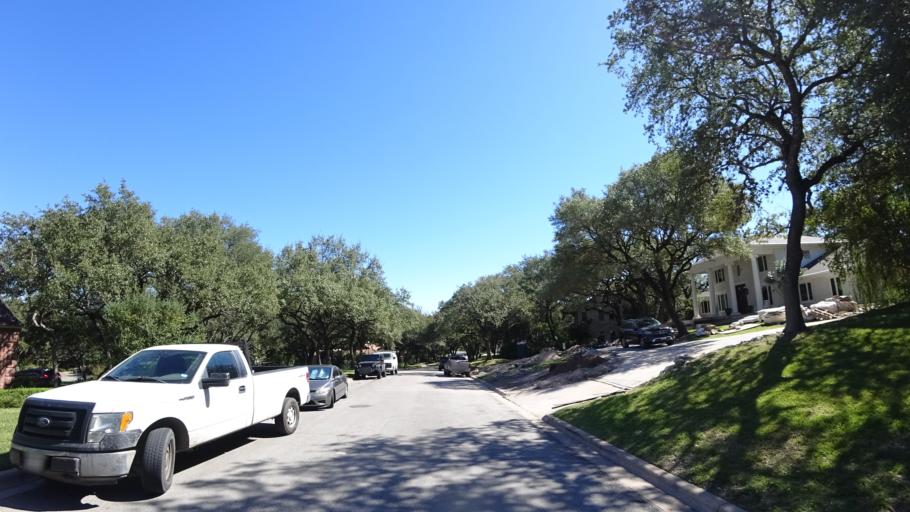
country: US
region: Texas
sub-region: Travis County
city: West Lake Hills
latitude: 30.3096
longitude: -97.7866
